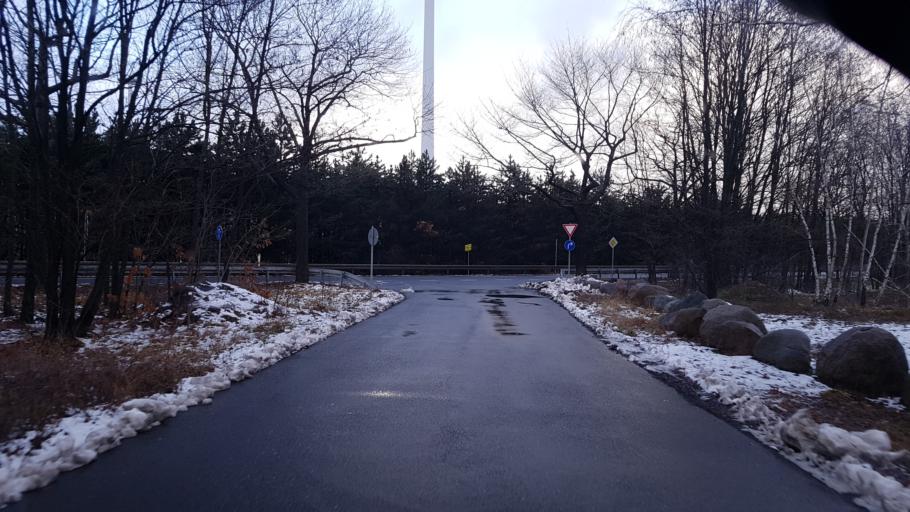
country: DE
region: Brandenburg
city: Heinersbruck
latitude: 51.7879
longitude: 14.4757
